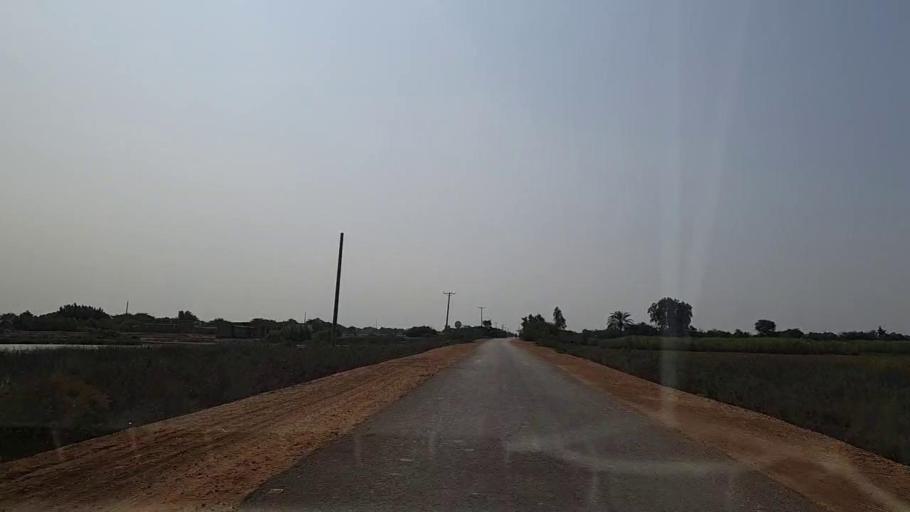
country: PK
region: Sindh
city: Chuhar Jamali
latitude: 24.3067
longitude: 67.9368
